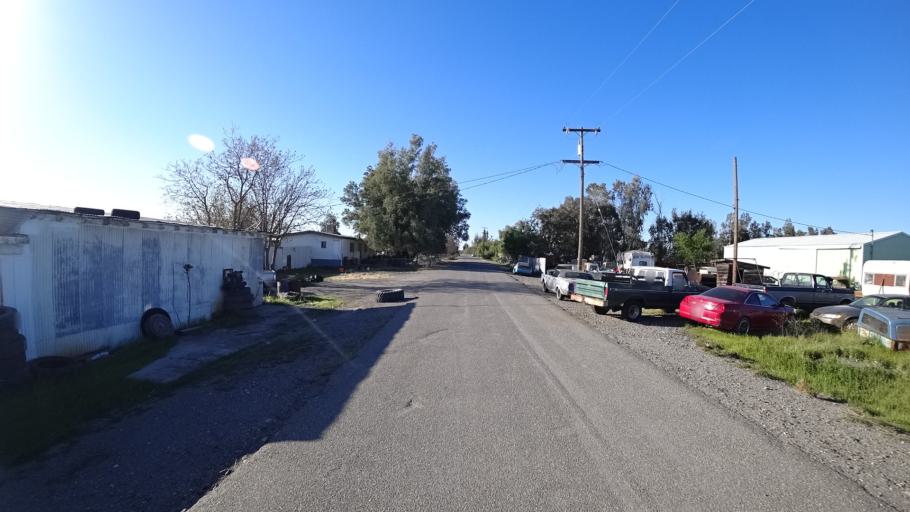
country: US
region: California
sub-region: Glenn County
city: Orland
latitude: 39.7583
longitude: -122.2270
